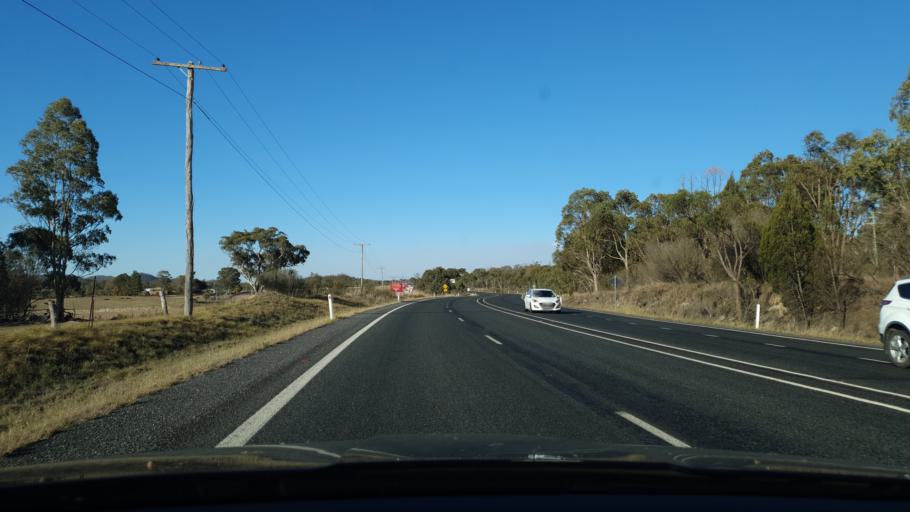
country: AU
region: Queensland
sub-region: Southern Downs
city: Stanthorpe
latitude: -28.6908
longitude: 151.9086
